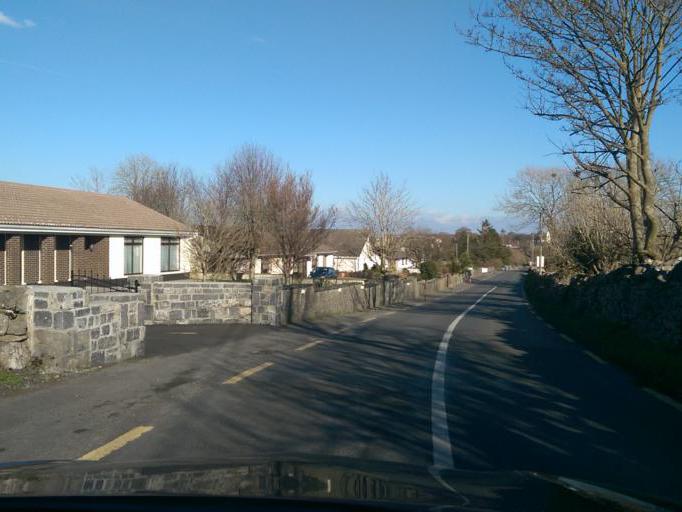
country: IE
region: Connaught
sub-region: County Galway
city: Oranmore
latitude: 53.2291
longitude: -8.8889
